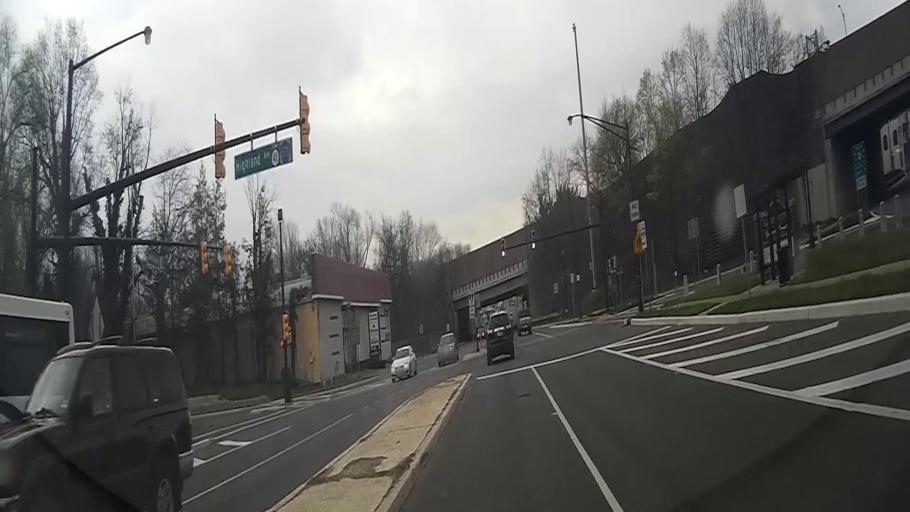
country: US
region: New Jersey
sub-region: Camden County
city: Barrington
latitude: 39.8763
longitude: -75.0497
